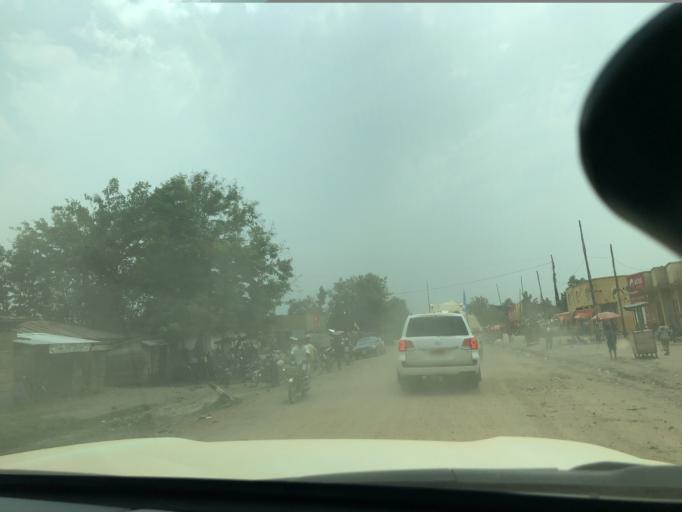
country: UG
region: Western Region
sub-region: Kasese District
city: Margherita
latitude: 0.3306
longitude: 29.6749
